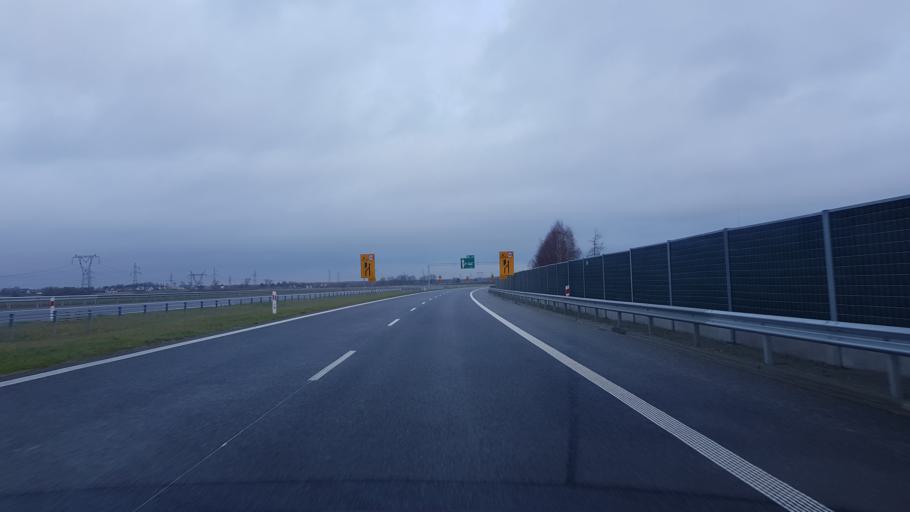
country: PL
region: West Pomeranian Voivodeship
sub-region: Koszalin
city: Koszalin
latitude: 54.2263
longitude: 16.1673
